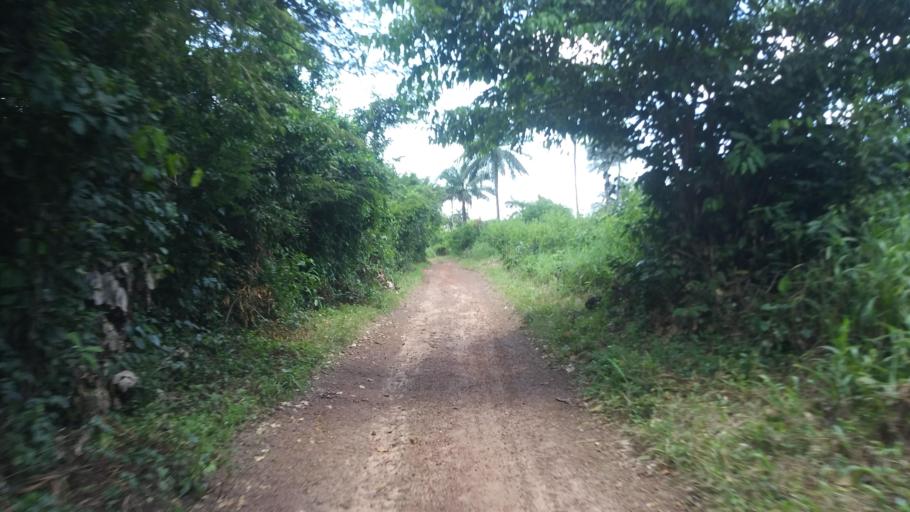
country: SL
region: Northern Province
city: Makeni
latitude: 8.8978
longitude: -11.9969
